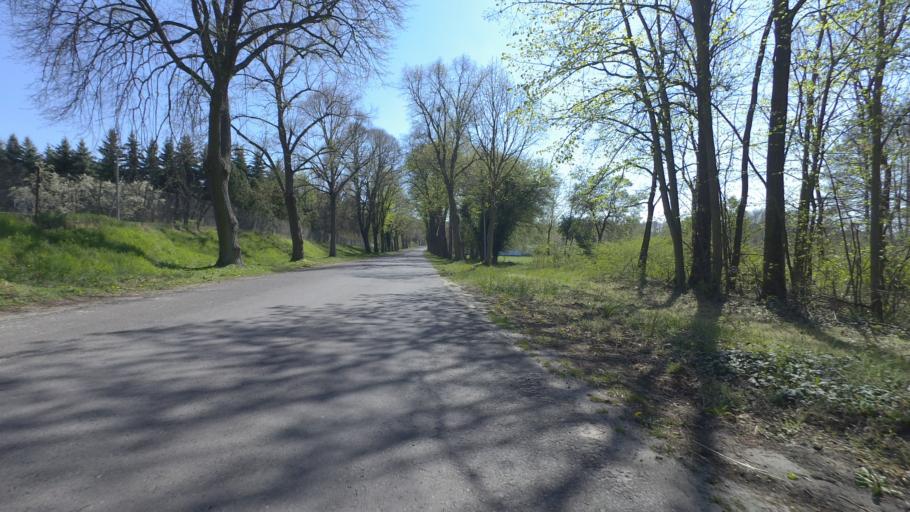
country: DE
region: Brandenburg
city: Zossen
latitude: 52.2031
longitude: 13.4674
